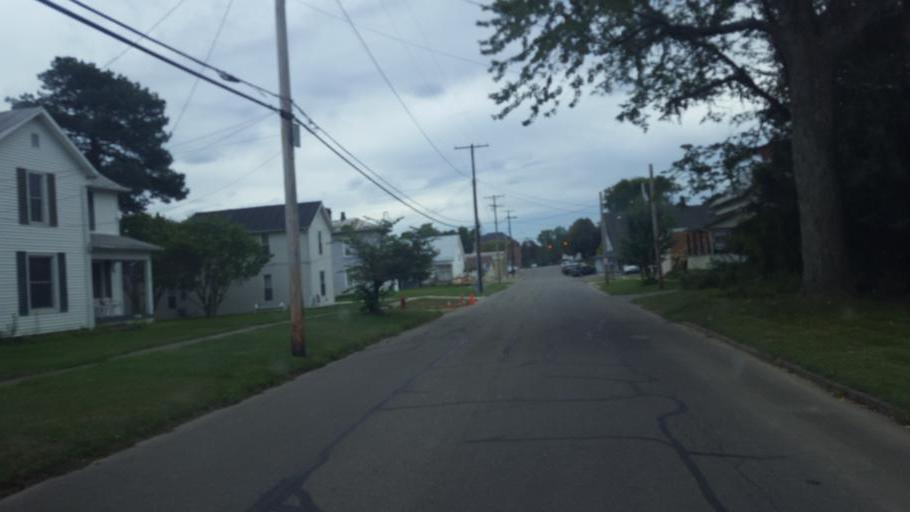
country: US
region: Ohio
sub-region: Knox County
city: Centerburg
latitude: 40.3063
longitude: -82.6969
